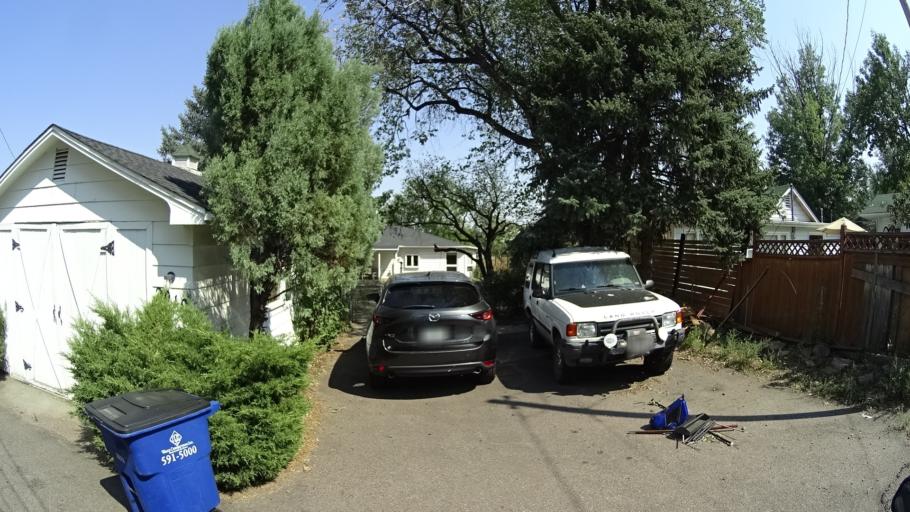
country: US
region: Colorado
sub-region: El Paso County
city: Colorado Springs
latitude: 38.8043
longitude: -104.8248
